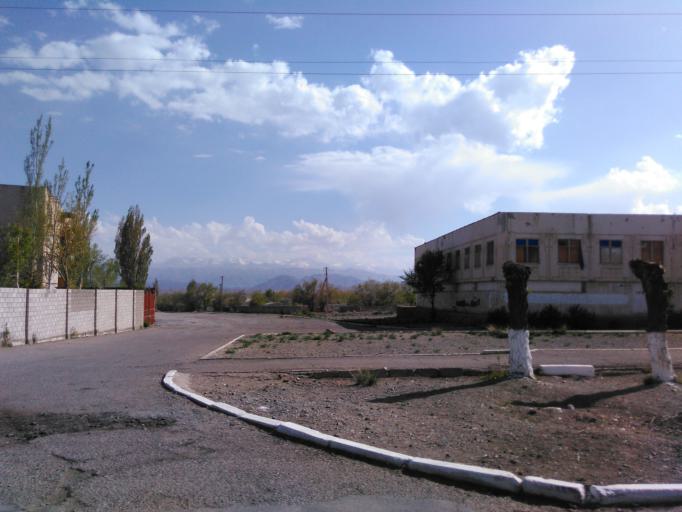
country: KG
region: Ysyk-Koel
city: Balykchy
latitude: 42.4520
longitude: 76.1680
